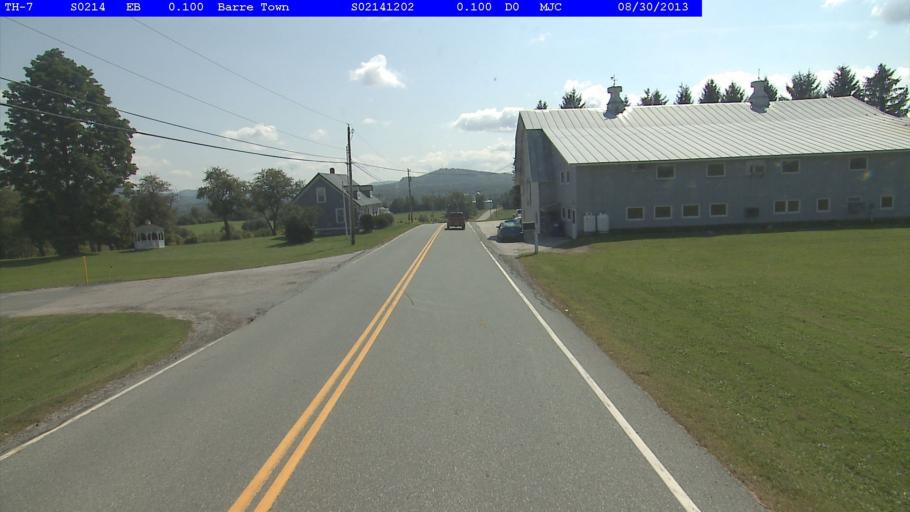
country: US
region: Vermont
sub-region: Washington County
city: South Barre
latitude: 44.1883
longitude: -72.5236
